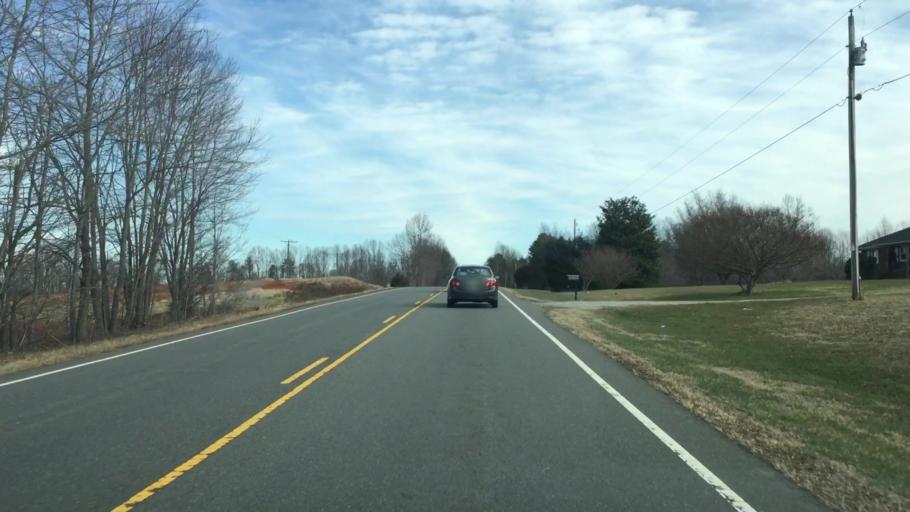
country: US
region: North Carolina
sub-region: Forsyth County
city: Walkertown
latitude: 36.1981
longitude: -80.0858
